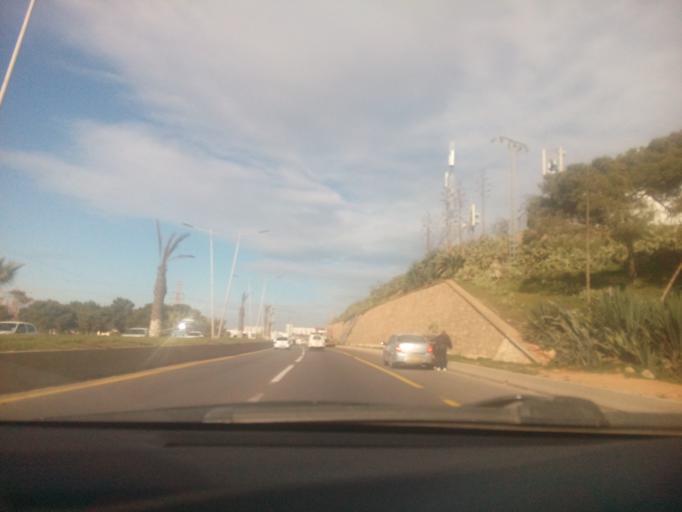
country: DZ
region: Oran
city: Es Senia
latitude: 35.6724
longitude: -0.5957
